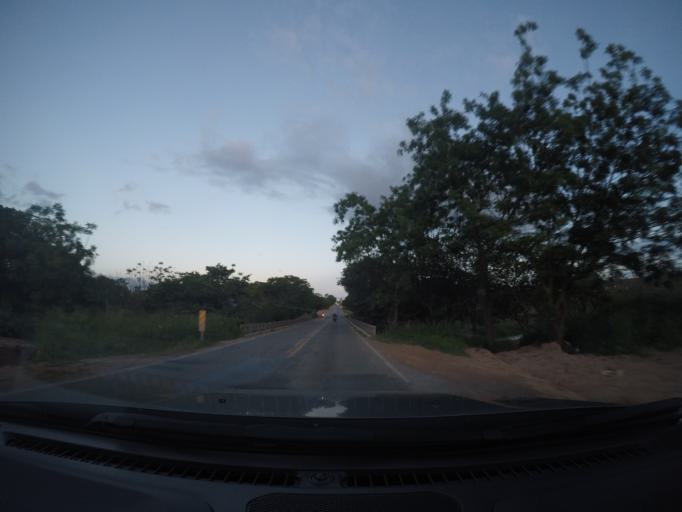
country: BR
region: Bahia
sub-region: Seabra
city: Seabra
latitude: -12.4284
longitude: -41.7772
